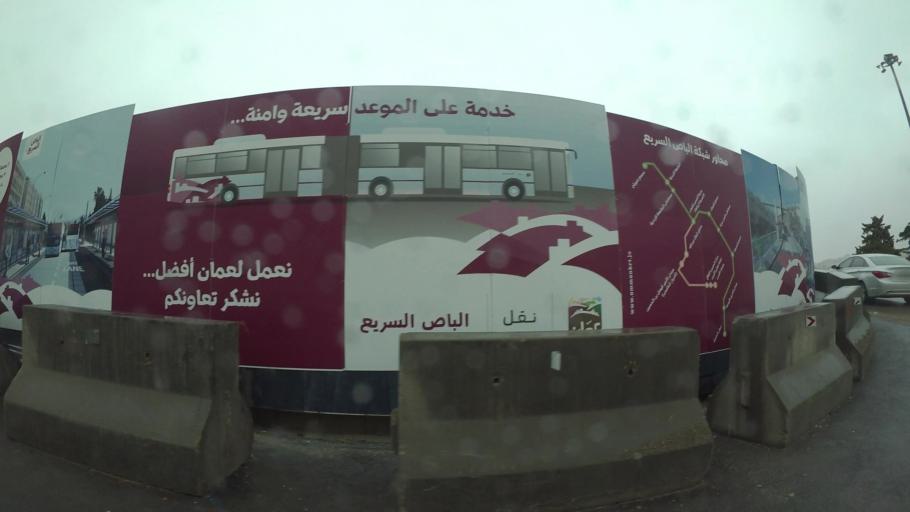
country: JO
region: Amman
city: Al Jubayhah
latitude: 32.0208
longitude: 35.8425
